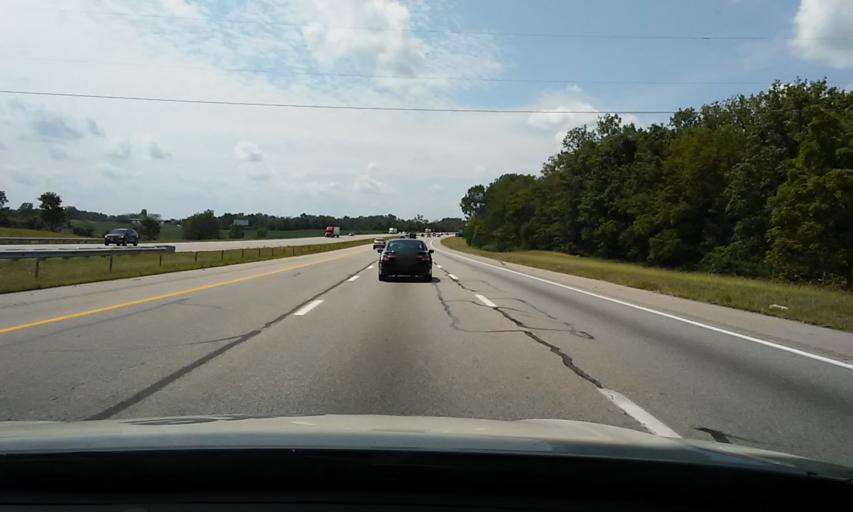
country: US
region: Ohio
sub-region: Clark County
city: Lisbon
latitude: 39.9340
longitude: -83.5897
